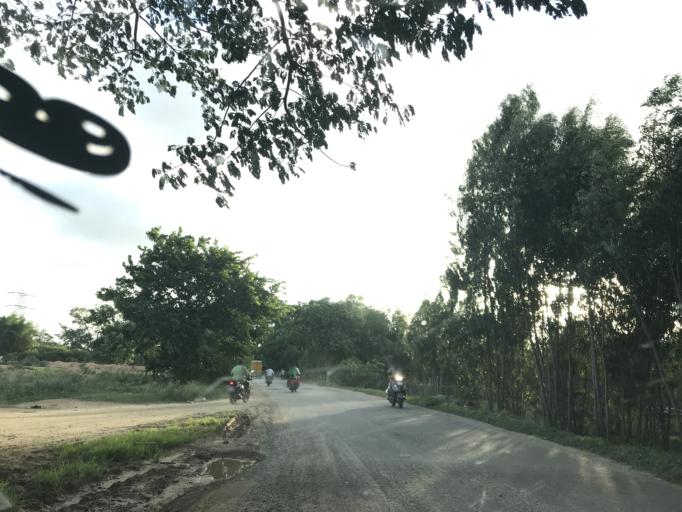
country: IN
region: Karnataka
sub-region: Bangalore Urban
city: Yelahanka
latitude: 13.1338
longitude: 77.6788
